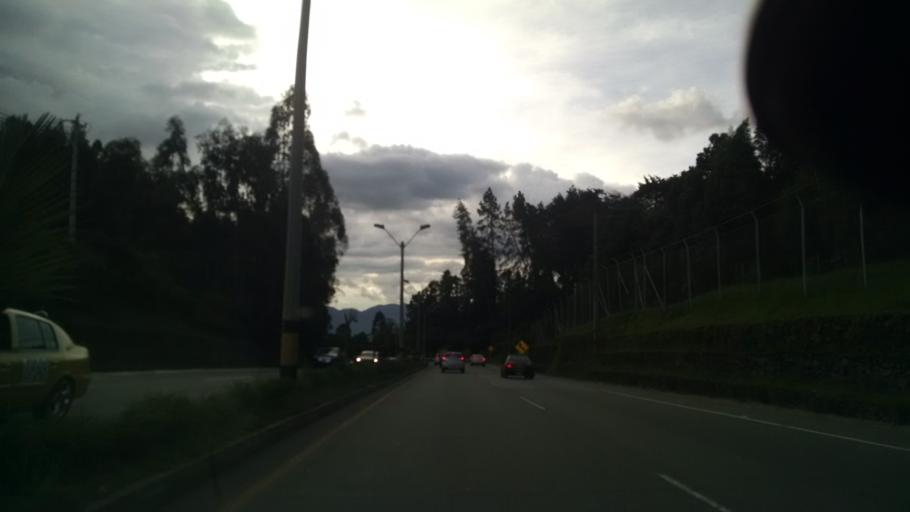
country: CO
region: Antioquia
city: Envigado
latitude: 6.1539
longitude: -75.5418
